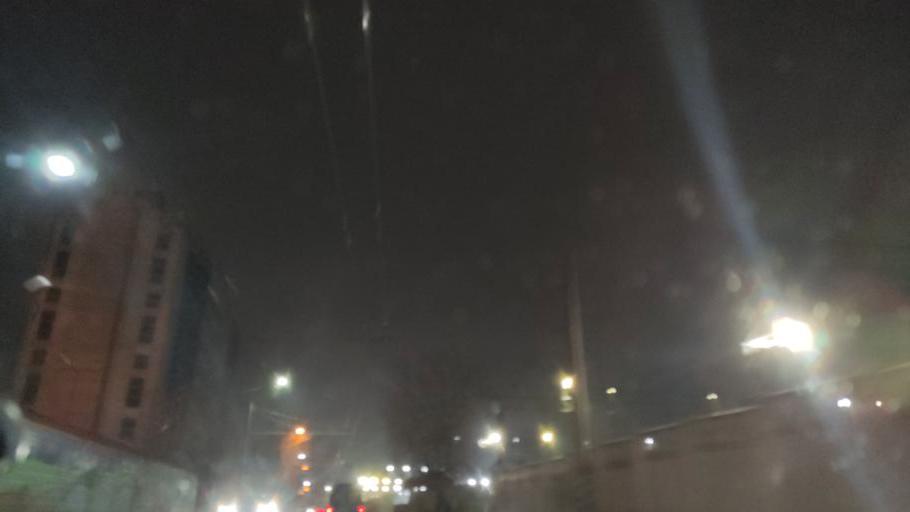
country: RU
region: Moskovskaya
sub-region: Podol'skiy Rayon
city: Podol'sk
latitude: 55.4291
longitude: 37.5651
